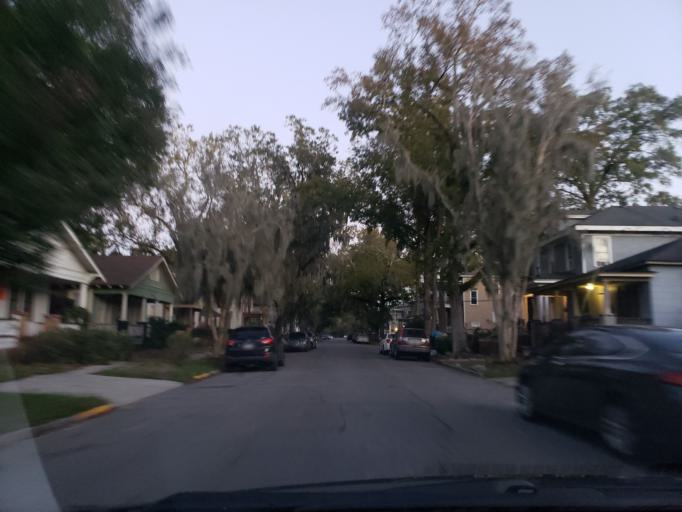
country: US
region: Georgia
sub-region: Chatham County
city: Savannah
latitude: 32.0570
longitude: -81.0809
